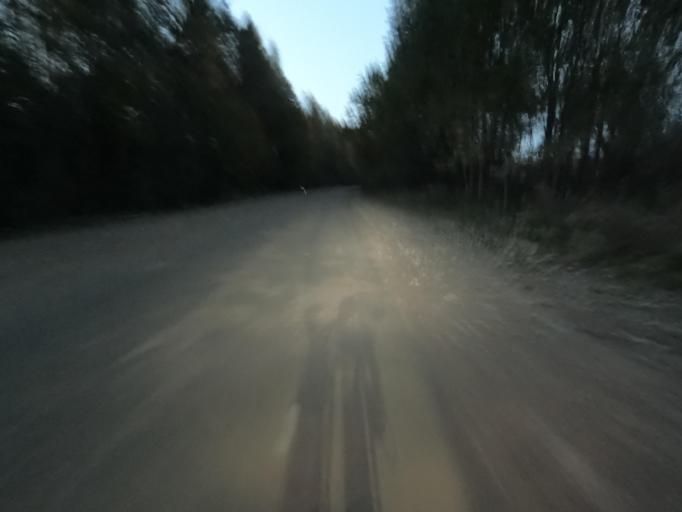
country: RU
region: Leningrad
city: Lyuban'
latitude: 59.1904
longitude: 31.2511
